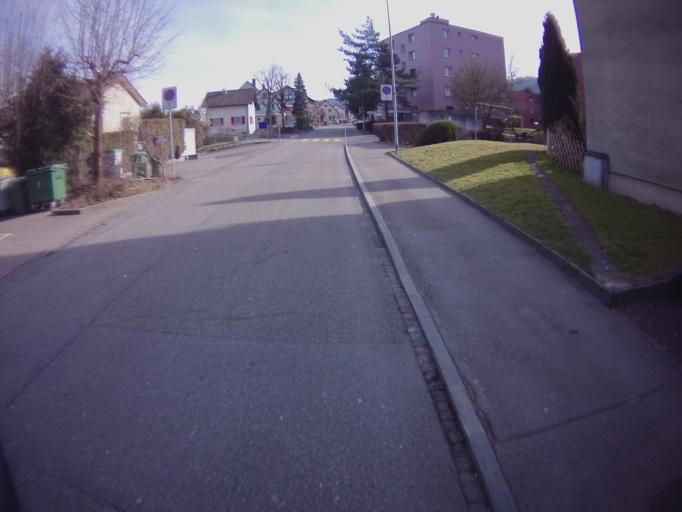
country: CH
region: Aargau
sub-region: Bezirk Baden
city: Neuenhof
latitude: 47.4498
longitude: 8.3312
